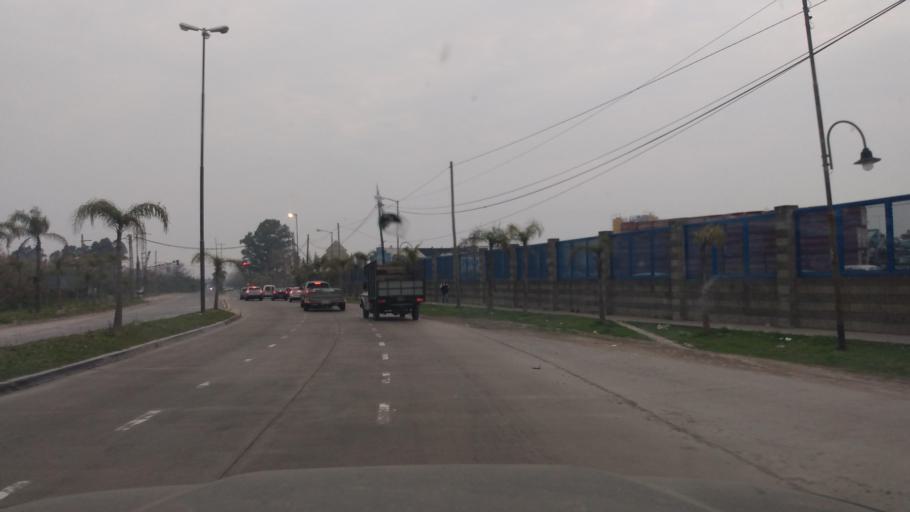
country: AR
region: Buenos Aires
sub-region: Partido de Tigre
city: Tigre
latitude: -34.4617
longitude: -58.5948
